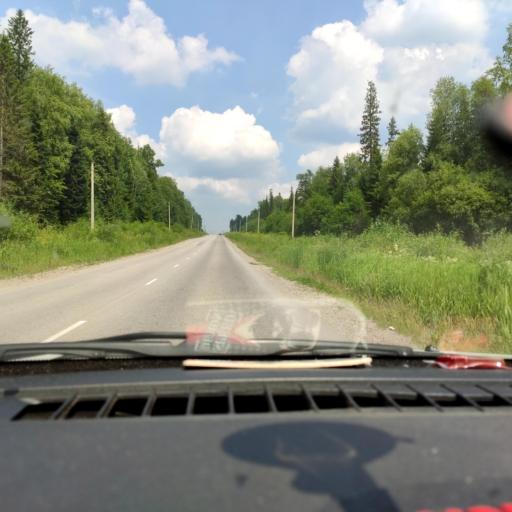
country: RU
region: Perm
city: Novyye Lyady
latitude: 57.9515
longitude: 56.5102
